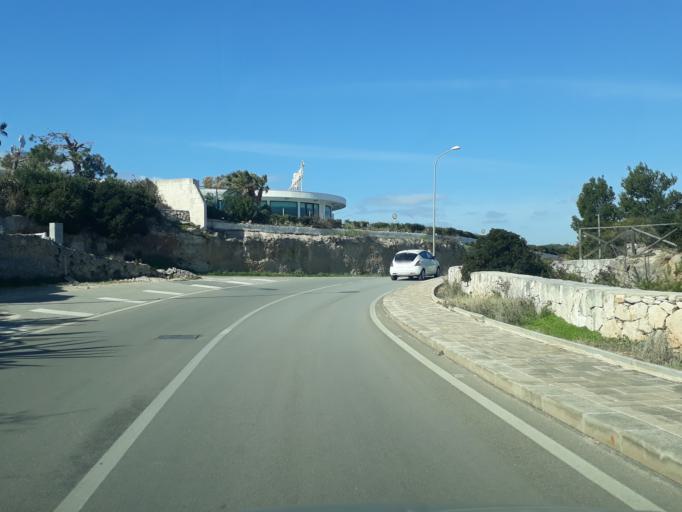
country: IT
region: Apulia
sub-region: Provincia di Bari
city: Monopoli
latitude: 40.9094
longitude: 17.3456
